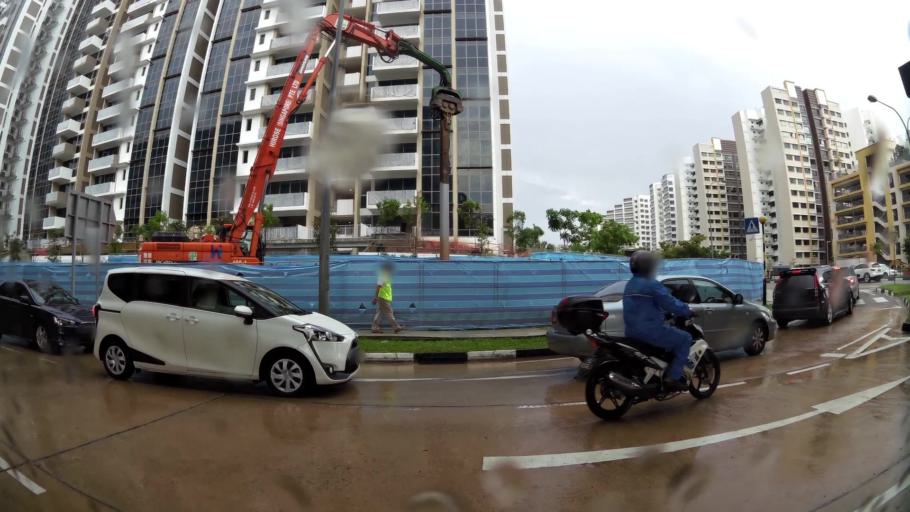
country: MY
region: Johor
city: Kampung Pasir Gudang Baru
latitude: 1.3963
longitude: 103.8944
